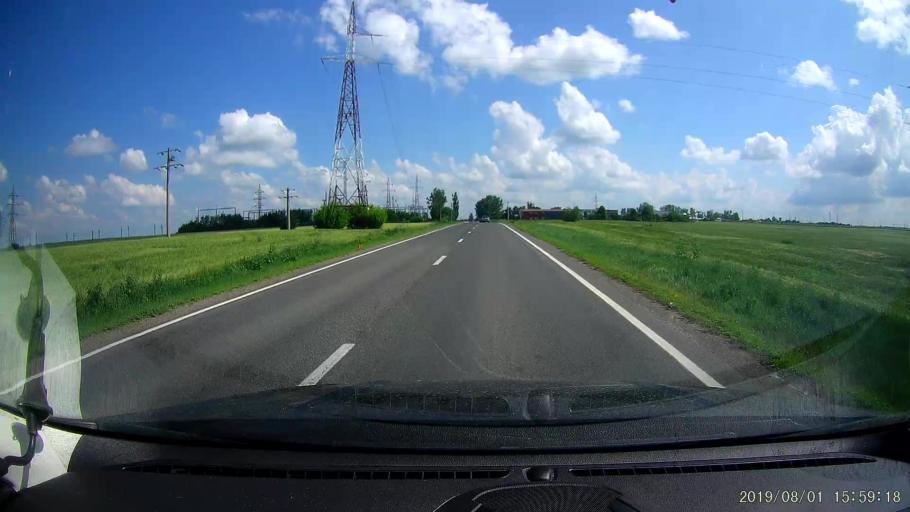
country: RO
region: Ialomita
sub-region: Comuna Slobozia
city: Slobozia
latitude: 44.5513
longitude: 27.3826
